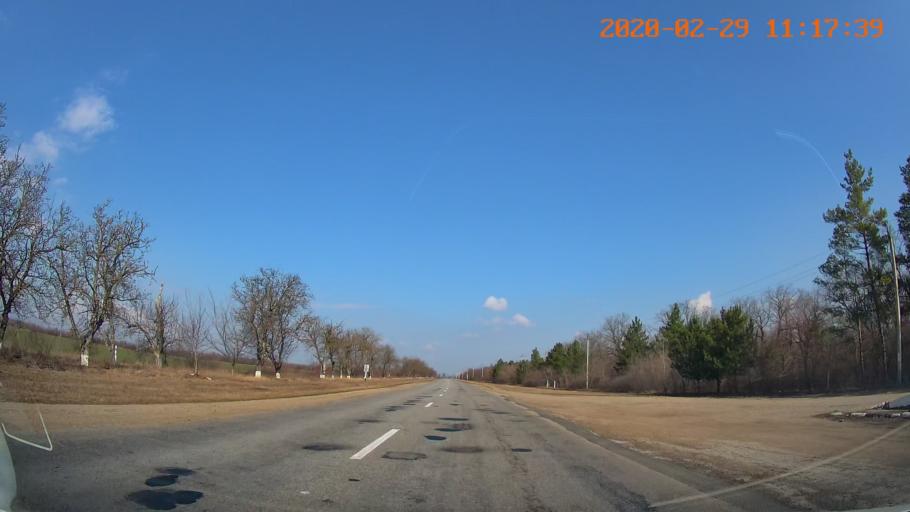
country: MD
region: Telenesti
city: Dubasari
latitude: 47.3246
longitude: 29.1712
